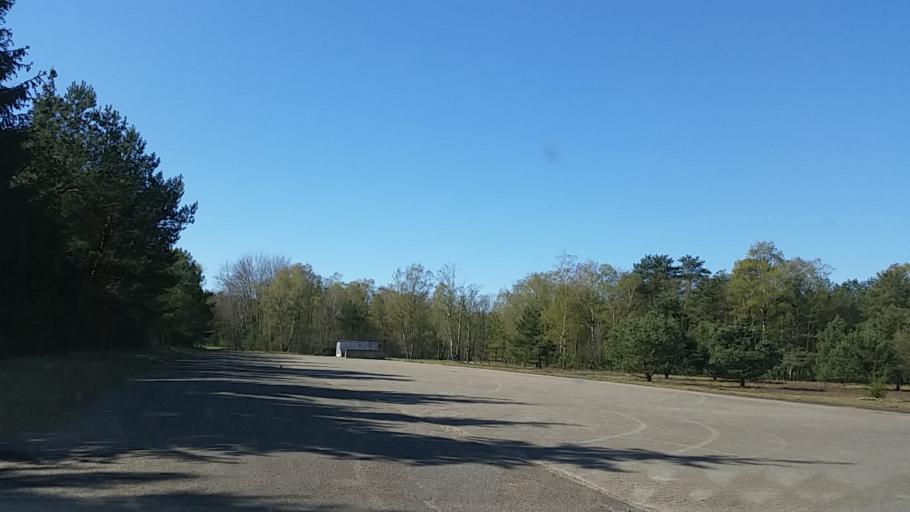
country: DE
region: Lower Saxony
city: Schneverdingen
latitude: 53.1443
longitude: 9.8205
